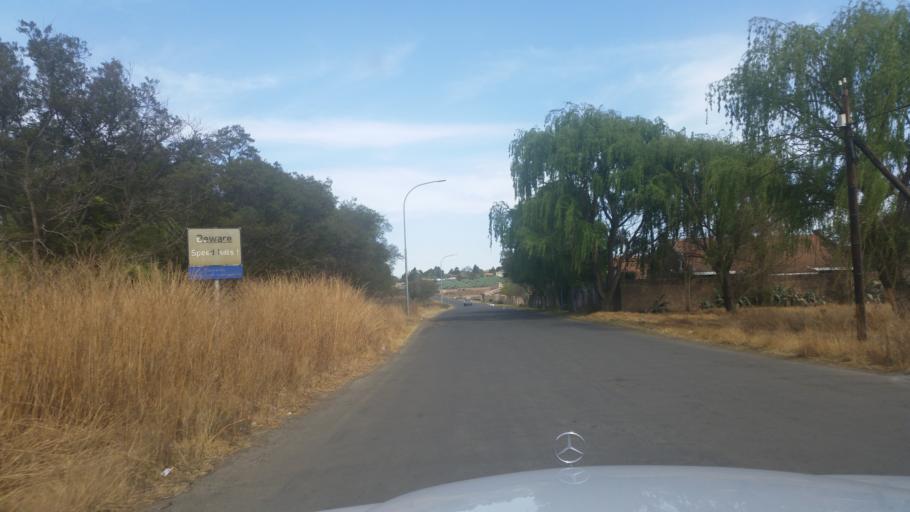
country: ZA
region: Orange Free State
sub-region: Thabo Mofutsanyana District Municipality
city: Harrismith
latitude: -28.2670
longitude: 29.1369
